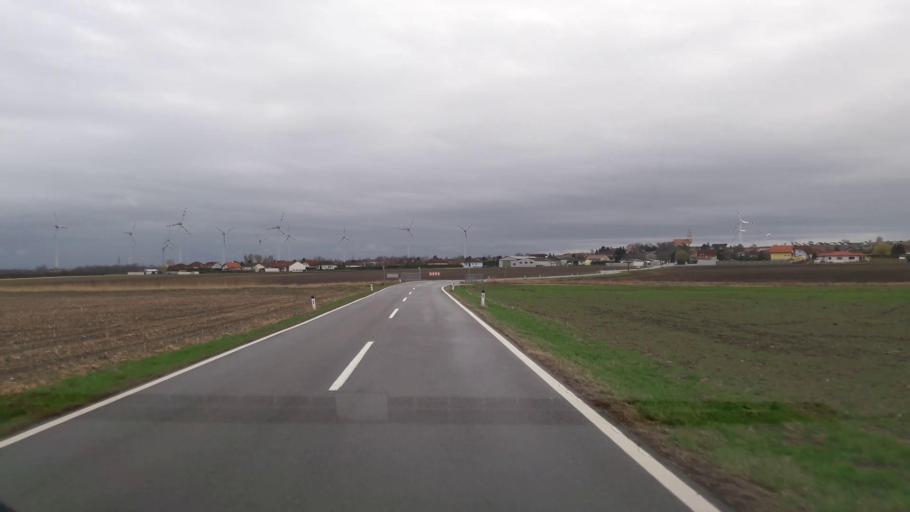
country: AT
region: Lower Austria
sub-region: Politischer Bezirk Bruck an der Leitha
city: Scharndorf
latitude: 48.0750
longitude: 16.7934
